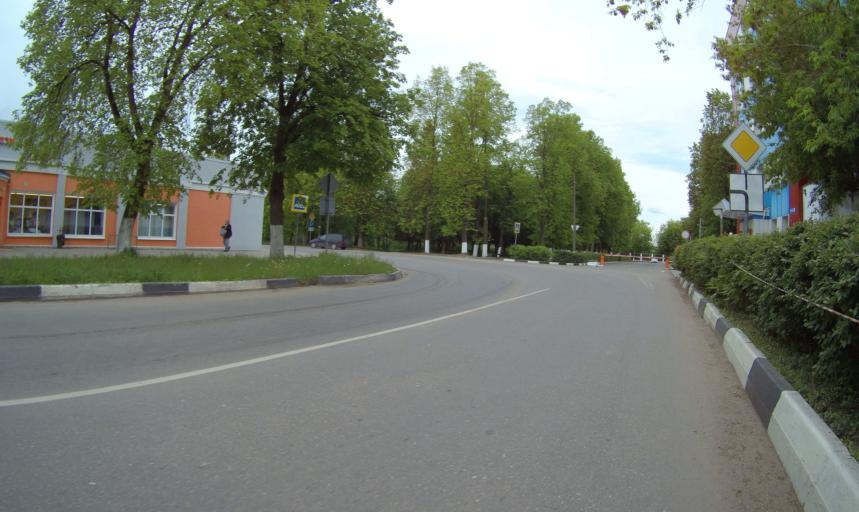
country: RU
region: Moskovskaya
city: Kolomna
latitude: 55.0710
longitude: 38.8034
